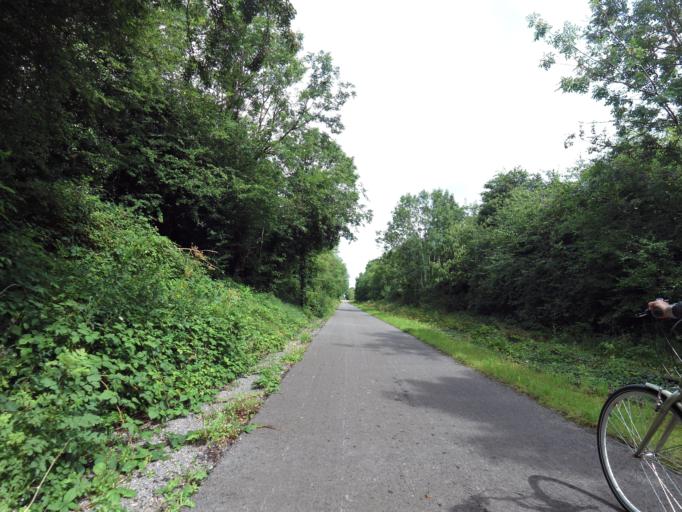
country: IE
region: Leinster
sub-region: An Iarmhi
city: Kilbeggan
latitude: 53.4743
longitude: -7.4852
